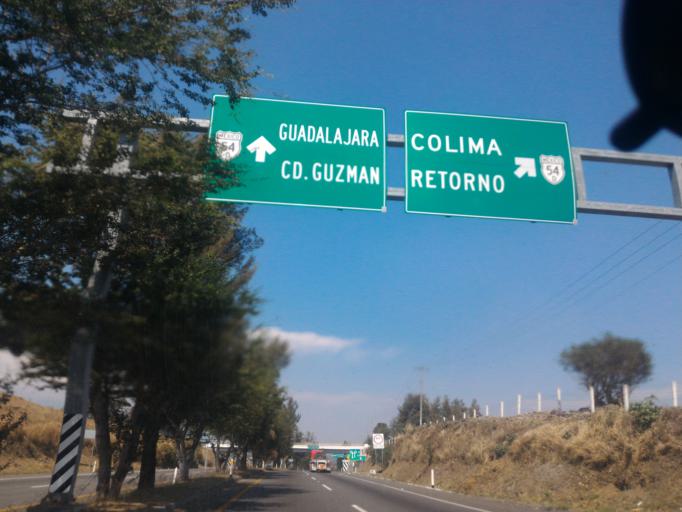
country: MX
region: Colima
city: Queseria
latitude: 19.3631
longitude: -103.5637
